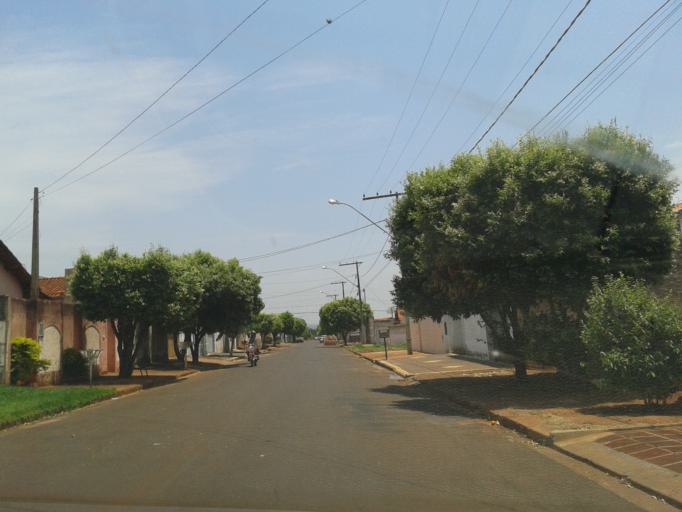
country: BR
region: Minas Gerais
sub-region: Ituiutaba
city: Ituiutaba
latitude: -18.9867
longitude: -49.4459
